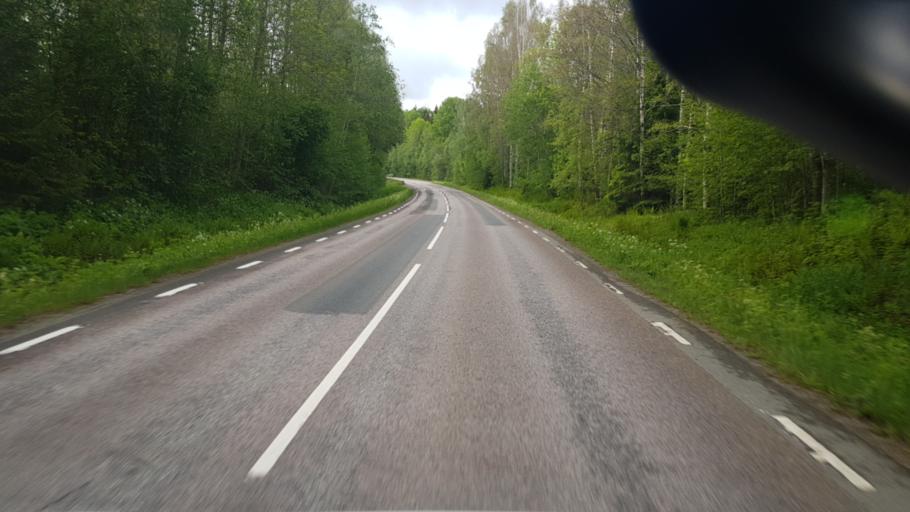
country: SE
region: Vaermland
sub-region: Eda Kommun
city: Amotfors
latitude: 59.6914
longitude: 12.3457
